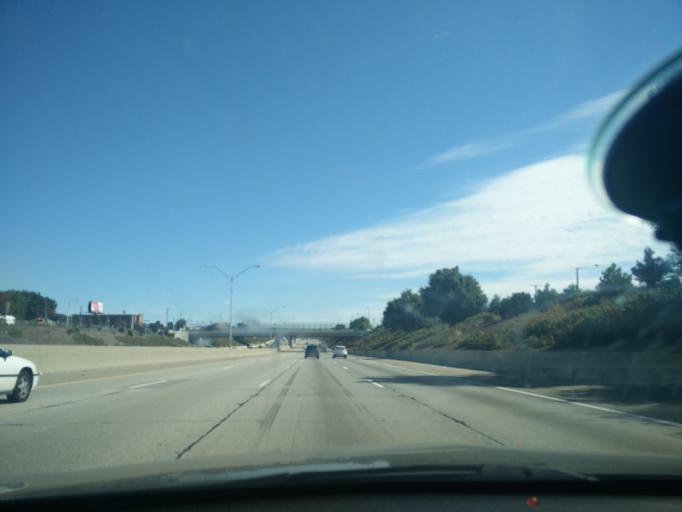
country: US
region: Michigan
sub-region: Macomb County
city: Center Line
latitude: 42.4915
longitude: -83.0318
